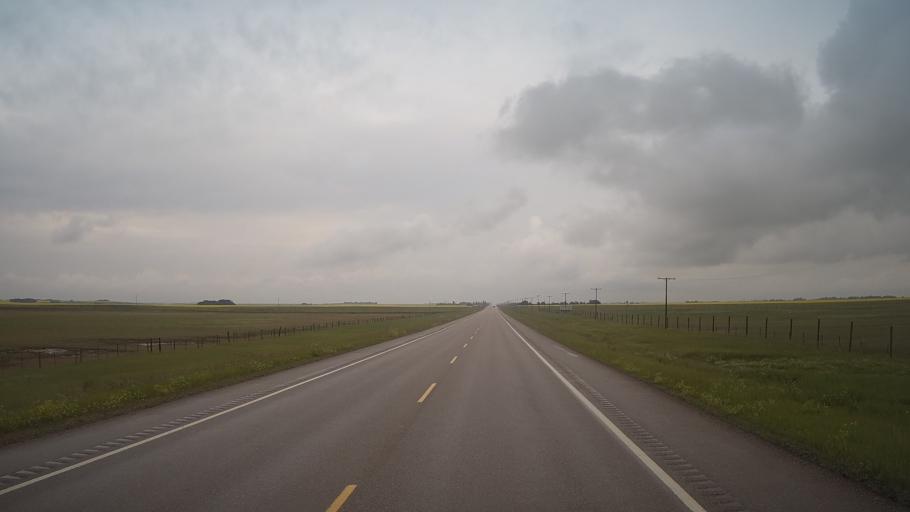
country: CA
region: Saskatchewan
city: Unity
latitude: 52.4349
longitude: -108.9943
